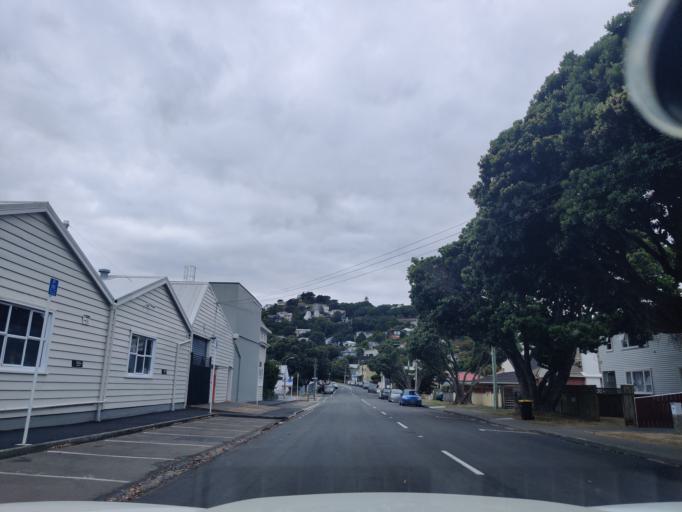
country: NZ
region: Wellington
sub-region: Wellington City
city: Wellington
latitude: -41.3063
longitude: 174.8235
